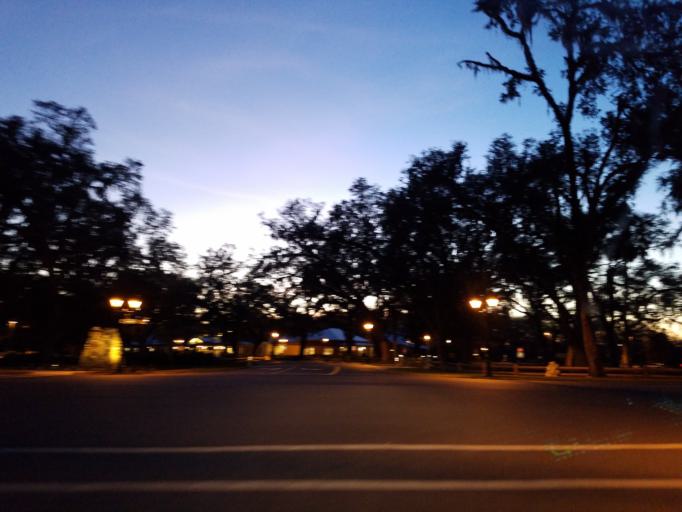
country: US
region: Florida
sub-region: Sumter County
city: Wildwood
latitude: 28.7969
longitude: -82.0373
